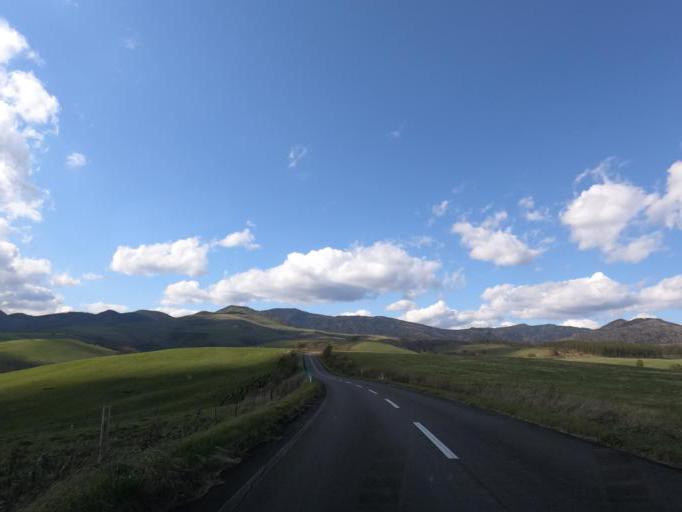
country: JP
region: Hokkaido
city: Otofuke
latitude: 43.2787
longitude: 143.2257
